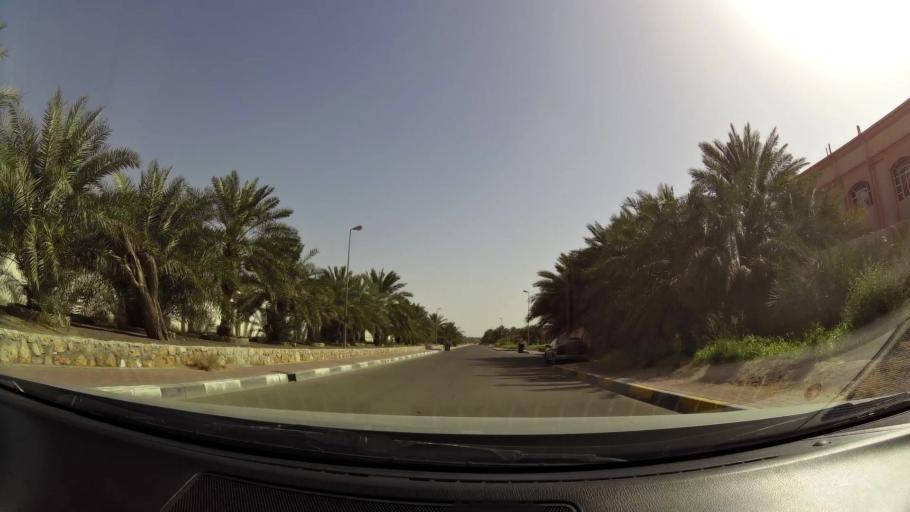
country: OM
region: Al Buraimi
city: Al Buraymi
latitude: 24.3164
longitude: 55.8039
